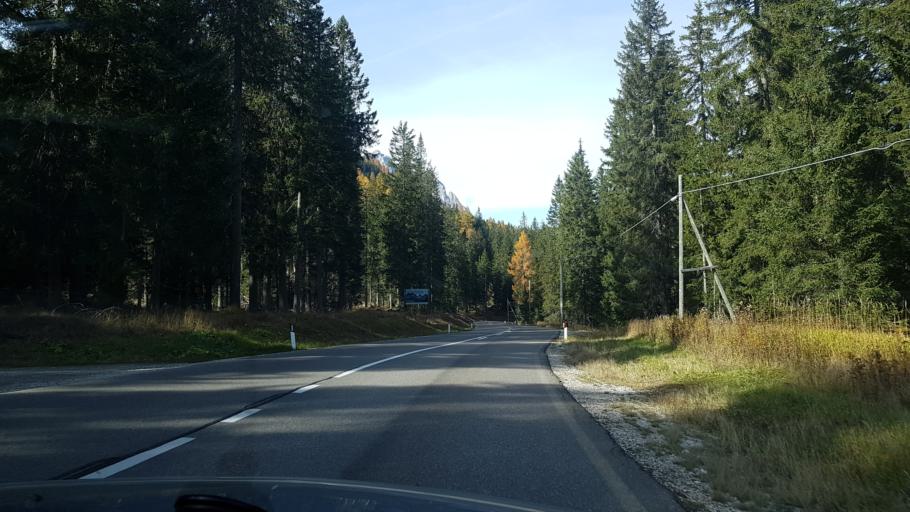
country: IT
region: Trentino-Alto Adige
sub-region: Bolzano
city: Sesto
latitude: 46.6598
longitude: 12.4071
